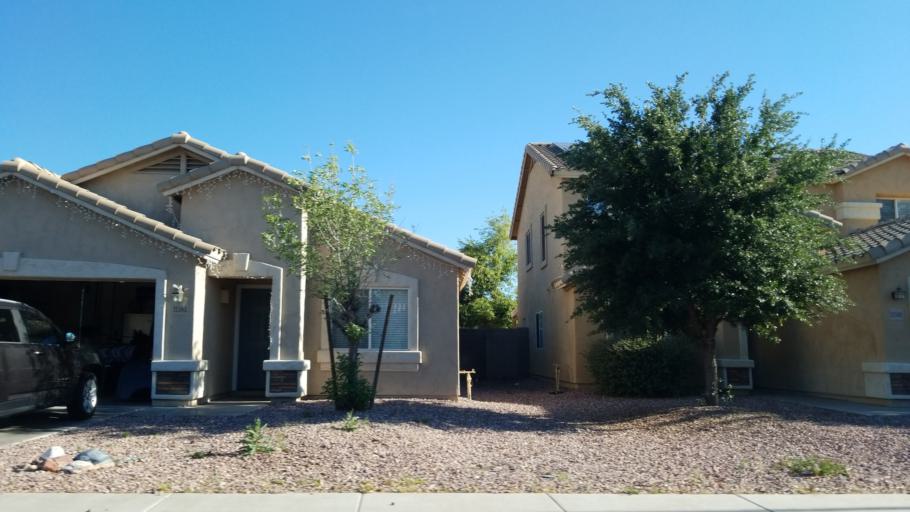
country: US
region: Arizona
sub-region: Maricopa County
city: Youngtown
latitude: 33.5780
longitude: -112.3091
